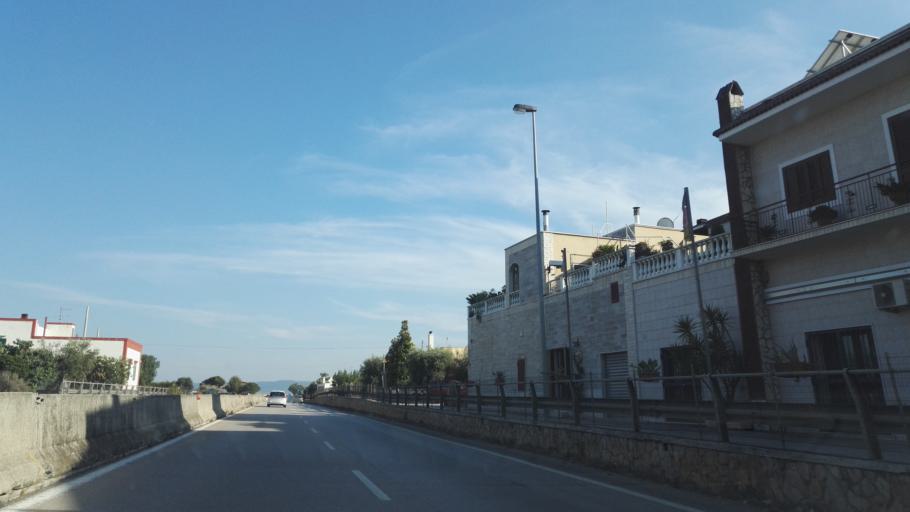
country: IT
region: Apulia
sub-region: Provincia di Brindisi
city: Fasano
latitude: 40.8801
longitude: 17.3383
